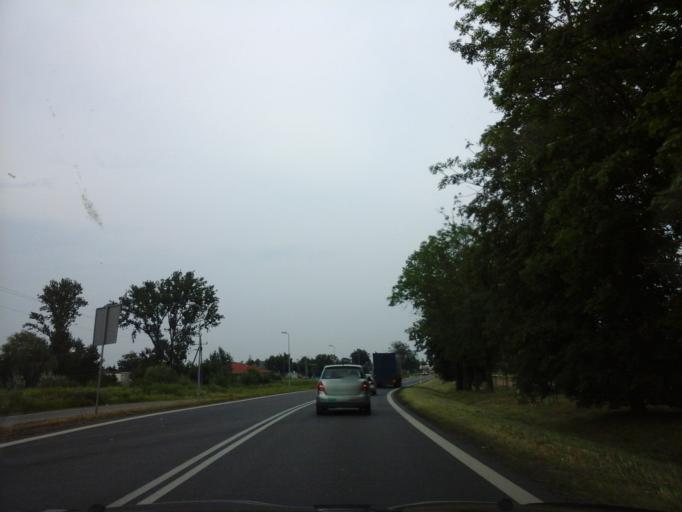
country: PL
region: Greater Poland Voivodeship
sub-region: Powiat grodziski
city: Grodzisk Wielkopolski
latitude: 52.2204
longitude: 16.3696
